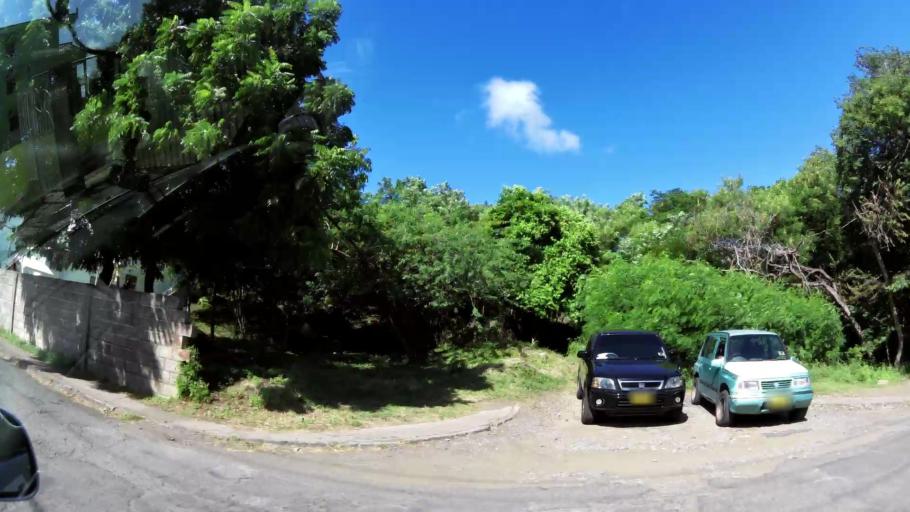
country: GD
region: Saint George
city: Saint George's
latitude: 12.0035
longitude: -61.7712
